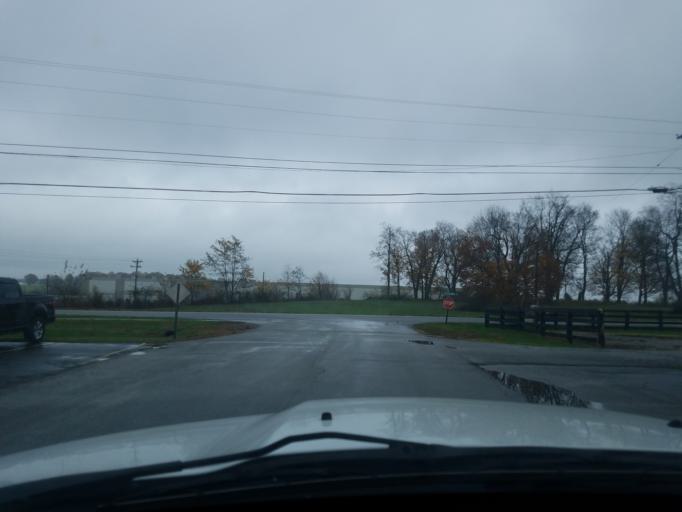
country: US
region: Kentucky
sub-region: Taylor County
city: Campbellsville
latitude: 37.3265
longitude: -85.3531
